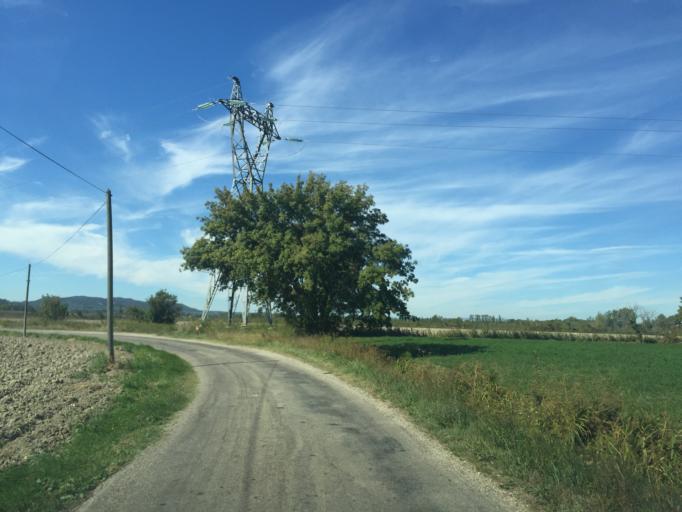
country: FR
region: Provence-Alpes-Cote d'Azur
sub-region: Departement du Vaucluse
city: Piolenc
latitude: 44.1566
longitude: 4.7496
